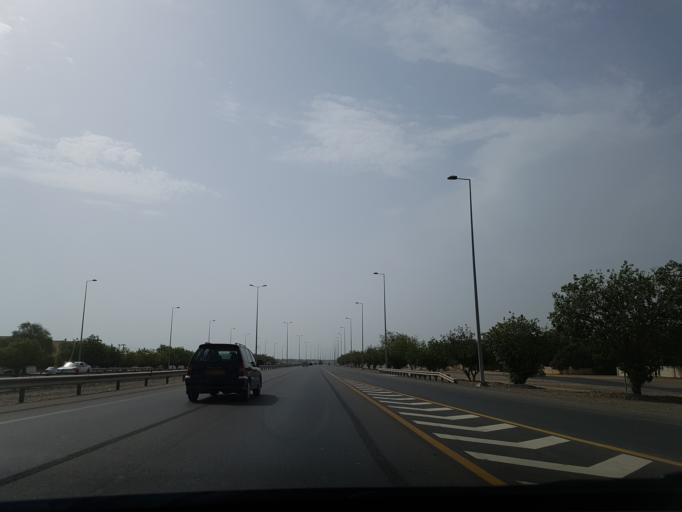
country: OM
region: Al Batinah
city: Saham
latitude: 24.1136
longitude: 56.9107
